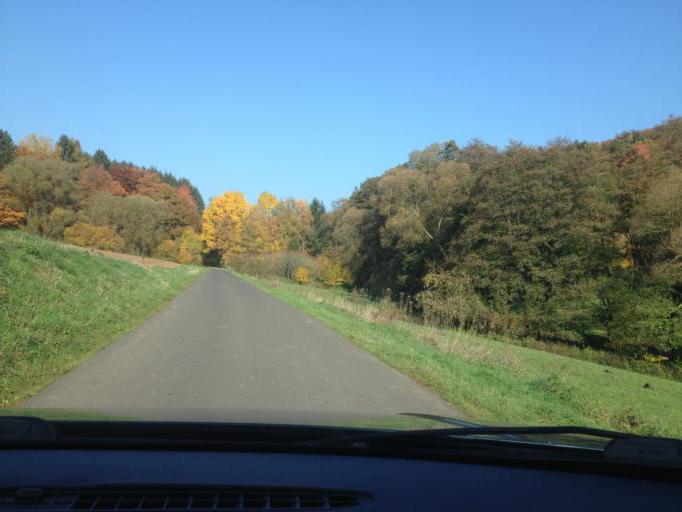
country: DE
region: Saarland
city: Sankt Wendel
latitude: 49.4870
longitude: 7.1824
